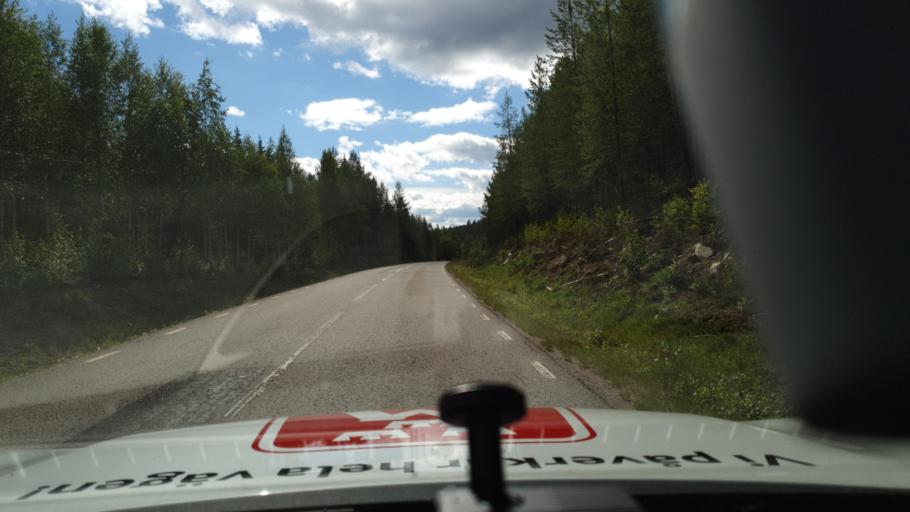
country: NO
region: Hedmark
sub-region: Trysil
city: Innbygda
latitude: 61.0263
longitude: 12.5592
